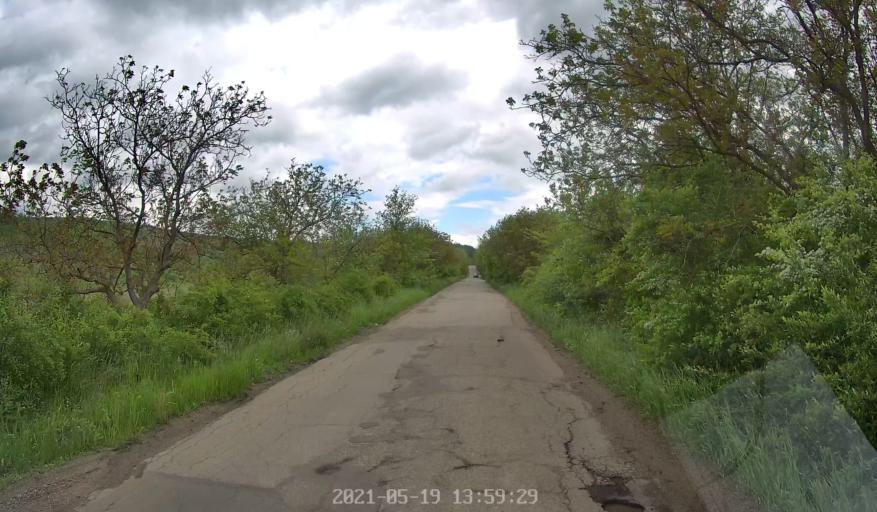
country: MD
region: Chisinau
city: Chisinau
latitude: 47.0400
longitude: 28.9241
